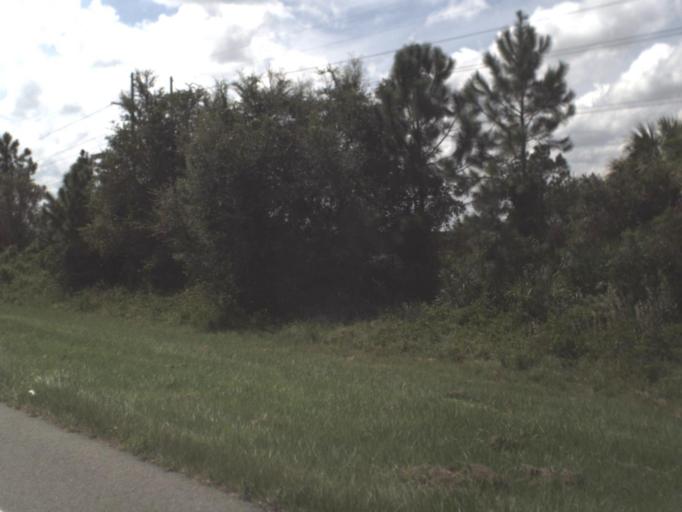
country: US
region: Florida
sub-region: Collier County
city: Immokalee
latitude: 26.3513
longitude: -81.3437
